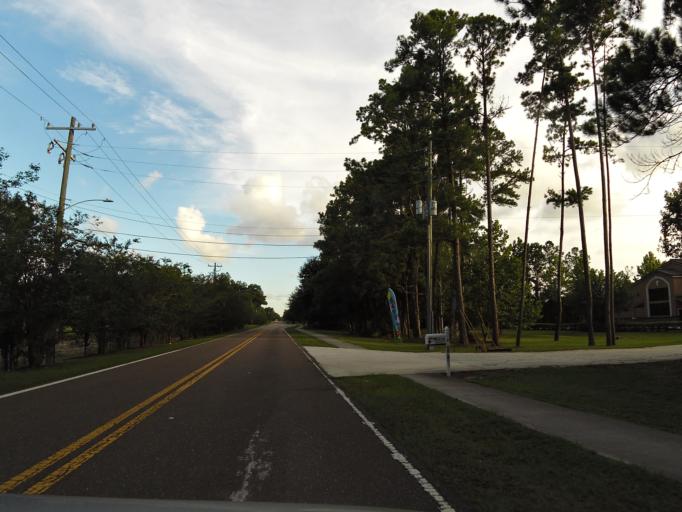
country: US
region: Florida
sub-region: Duval County
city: Jacksonville
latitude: 30.4127
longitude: -81.6974
